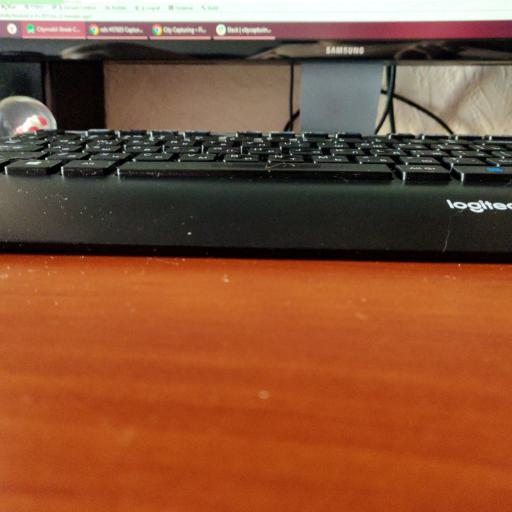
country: EE
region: Saare
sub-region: Kuressaare linn
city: Kuressaare
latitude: 58.5603
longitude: 22.5877
